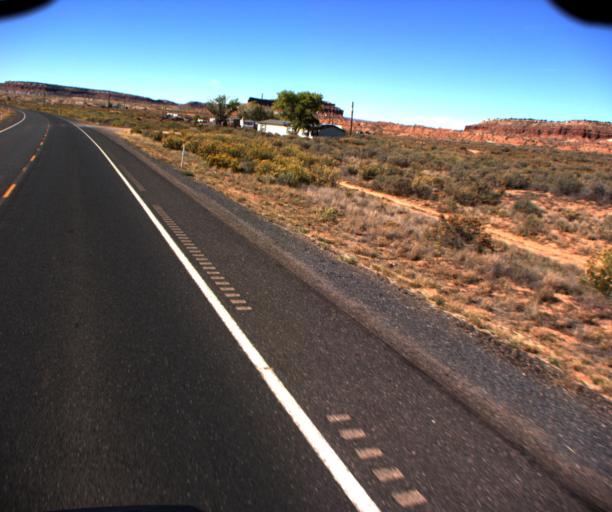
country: US
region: Arizona
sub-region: Coconino County
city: Fredonia
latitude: 36.9449
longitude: -112.5394
